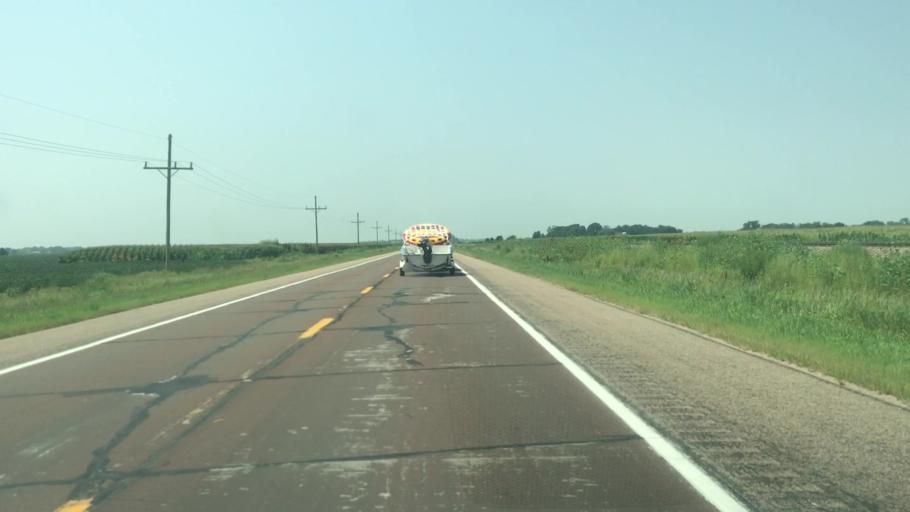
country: US
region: Nebraska
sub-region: Hall County
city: Grand Island
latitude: 40.9626
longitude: -98.4254
